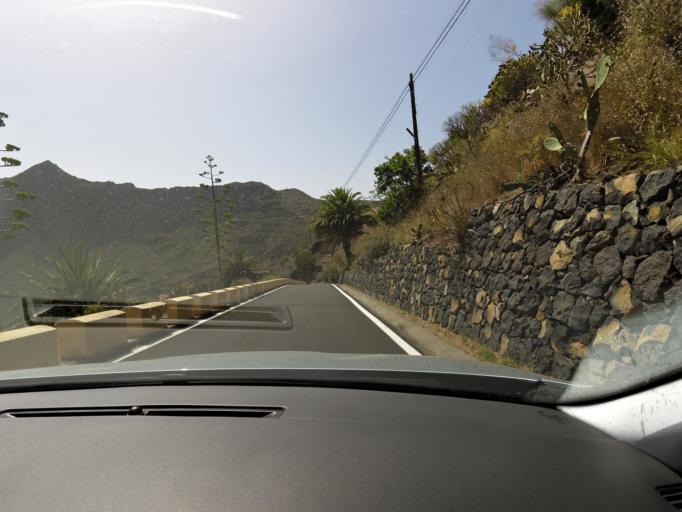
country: ES
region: Canary Islands
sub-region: Provincia de Santa Cruz de Tenerife
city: Santiago del Teide
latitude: 28.3043
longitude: -16.8382
